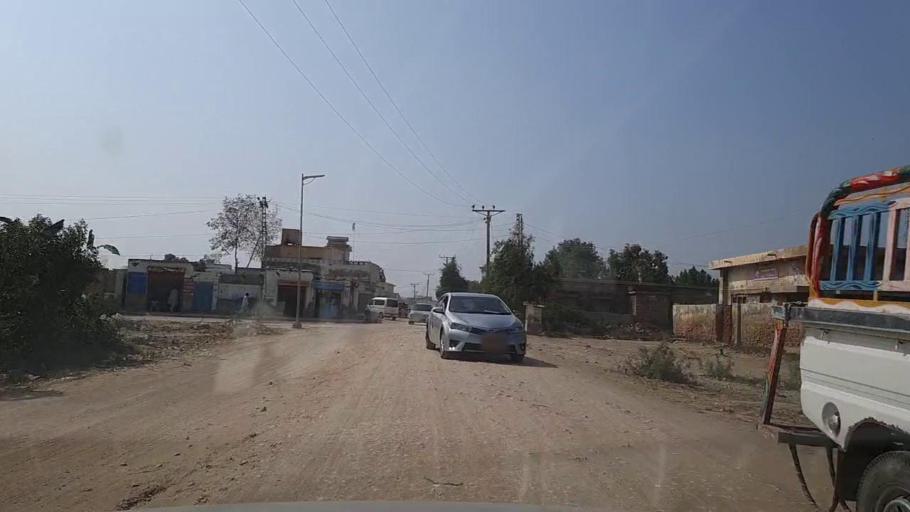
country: PK
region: Sindh
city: Mirpur Sakro
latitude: 24.5506
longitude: 67.6282
